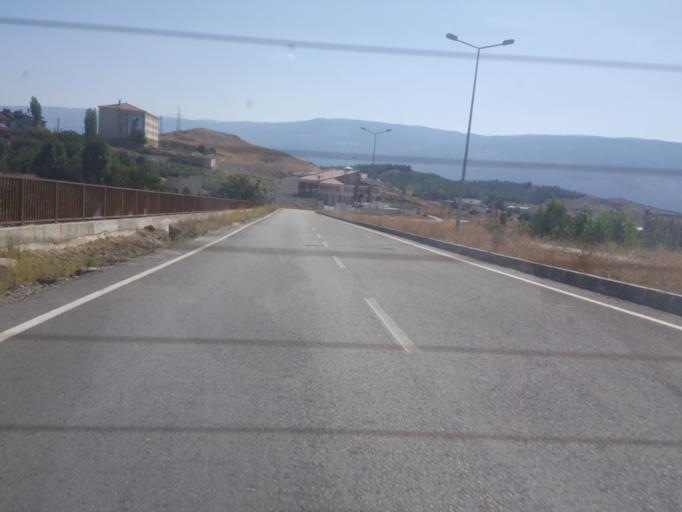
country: TR
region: Kastamonu
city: Tosya
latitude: 41.0063
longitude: 34.0631
